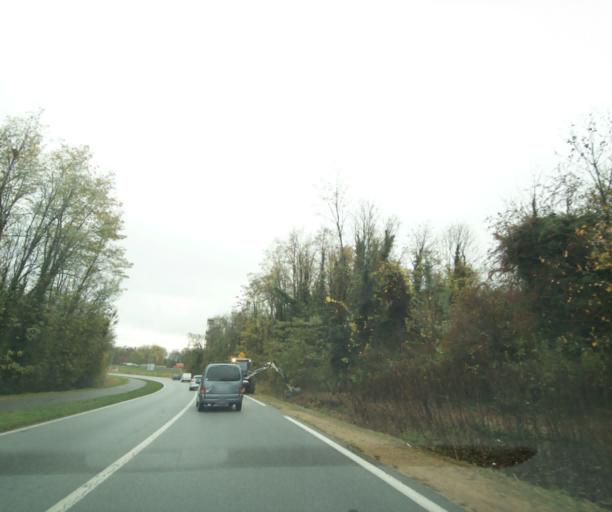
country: FR
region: Auvergne
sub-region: Departement du Puy-de-Dome
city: Cournon-d'Auvergne
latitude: 45.7487
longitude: 3.2109
